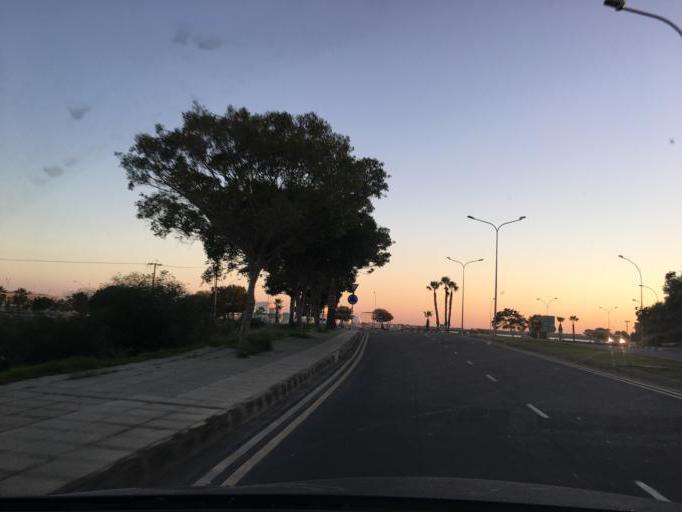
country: CY
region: Larnaka
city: Meneou
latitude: 34.8847
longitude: 33.6225
